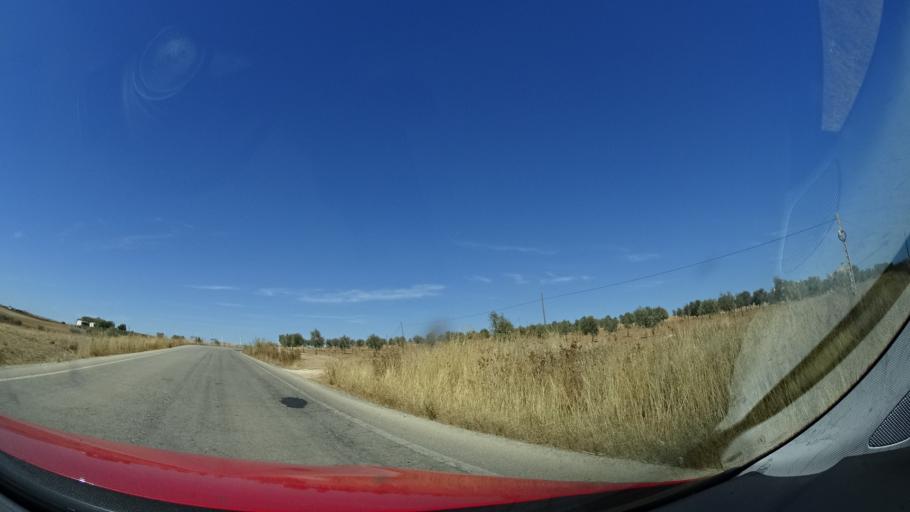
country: ES
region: Andalusia
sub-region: Provincia de Malaga
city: Campillos
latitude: 37.0724
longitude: -4.8632
